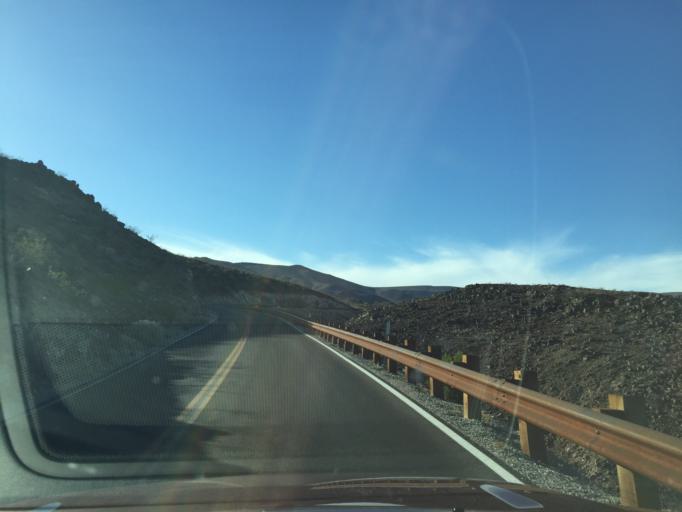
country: US
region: California
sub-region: San Bernardino County
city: Searles Valley
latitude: 36.3429
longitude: -117.5154
